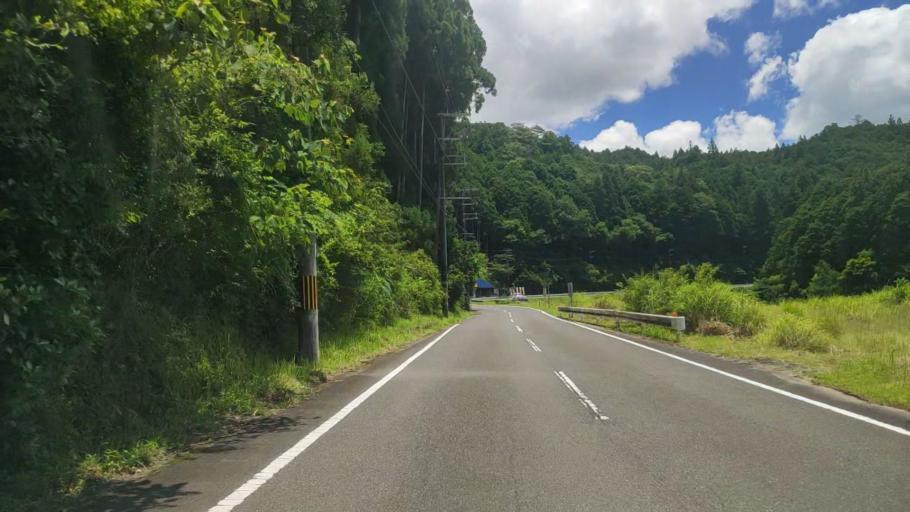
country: JP
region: Mie
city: Owase
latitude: 33.9628
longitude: 136.0647
